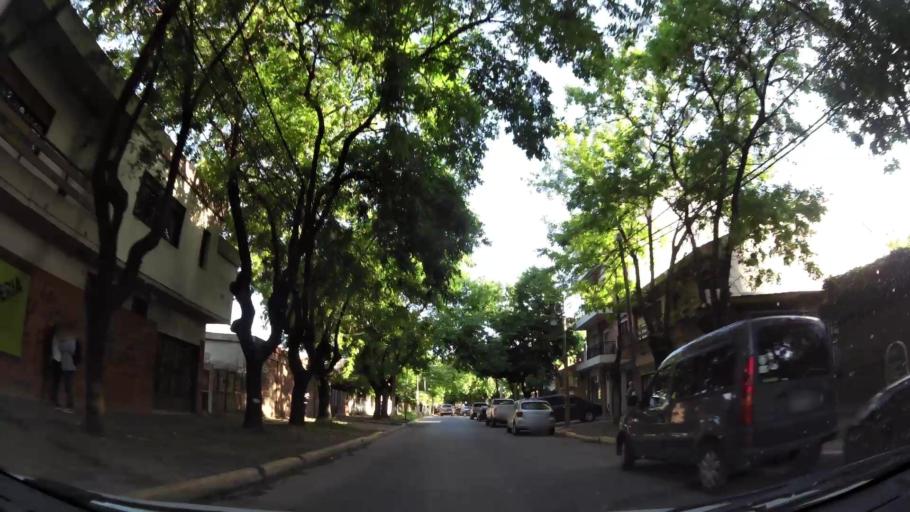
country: AR
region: Buenos Aires
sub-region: Partido de Merlo
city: Merlo
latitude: -34.6729
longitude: -58.7251
